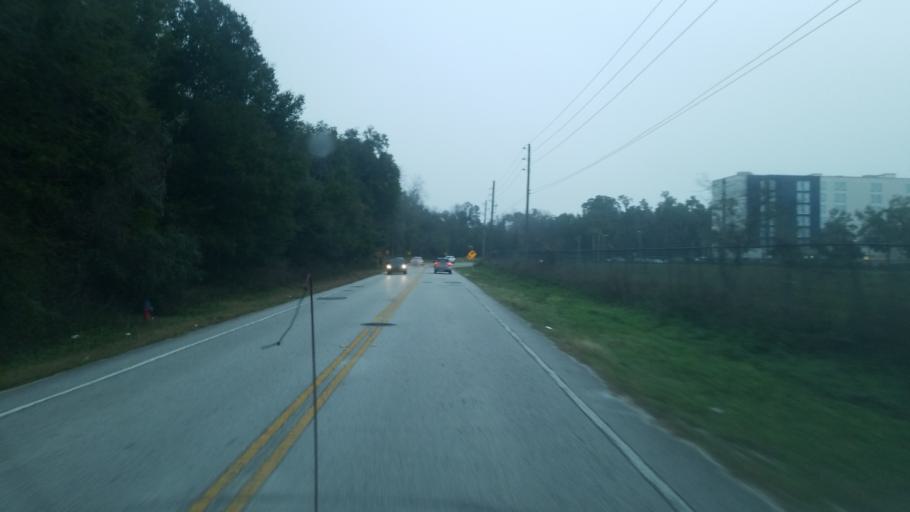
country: US
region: Florida
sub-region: Marion County
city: Ocala
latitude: 29.1489
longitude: -82.1921
